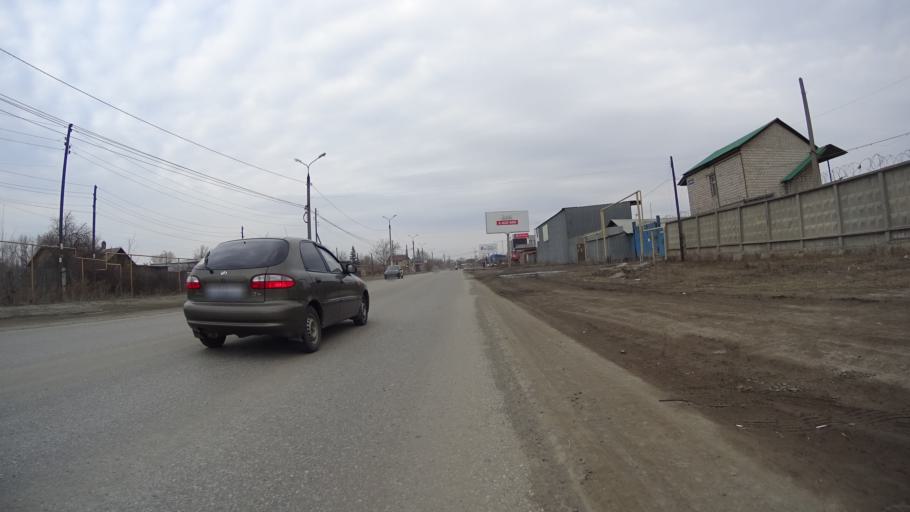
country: RU
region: Chelyabinsk
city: Zheleznodorozhnyy
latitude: 55.1579
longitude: 61.5163
